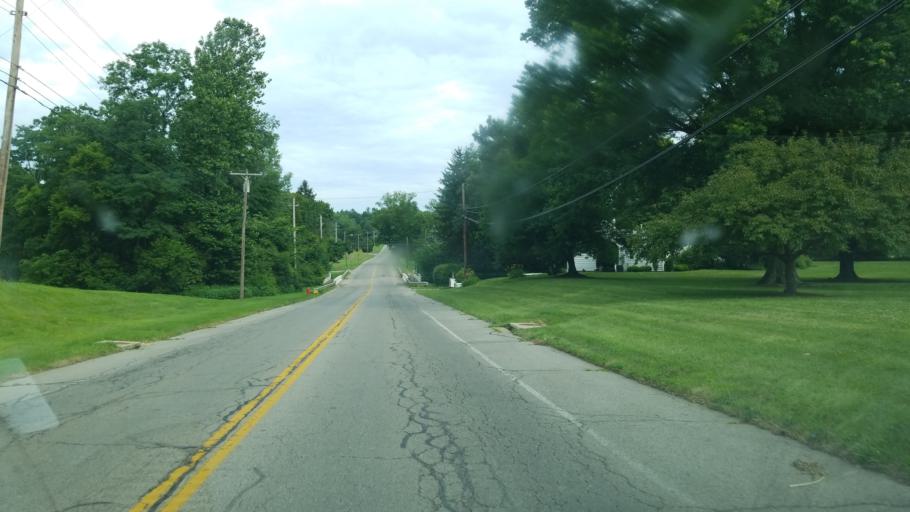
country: US
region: Ohio
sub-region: Ashland County
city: Ashland
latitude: 40.8495
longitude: -82.3018
